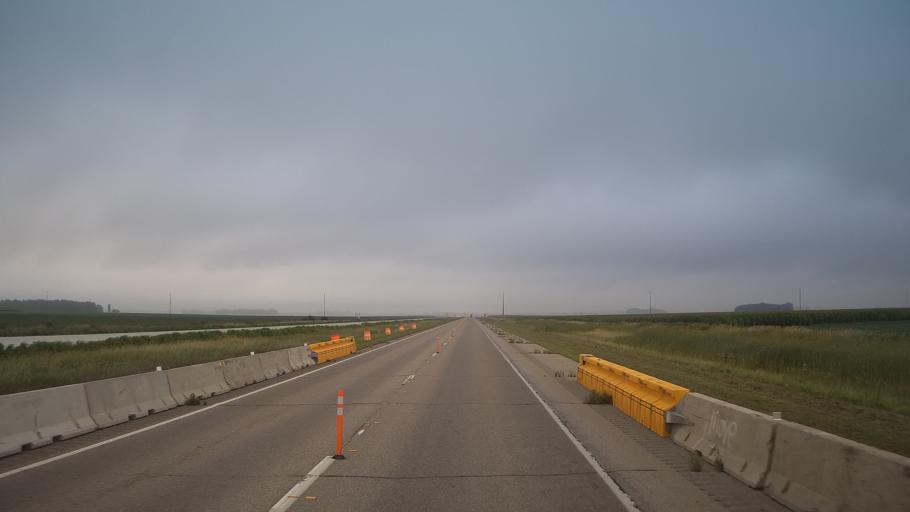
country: US
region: Minnesota
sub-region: Faribault County
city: Blue Earth
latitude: 43.6665
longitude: -94.1768
